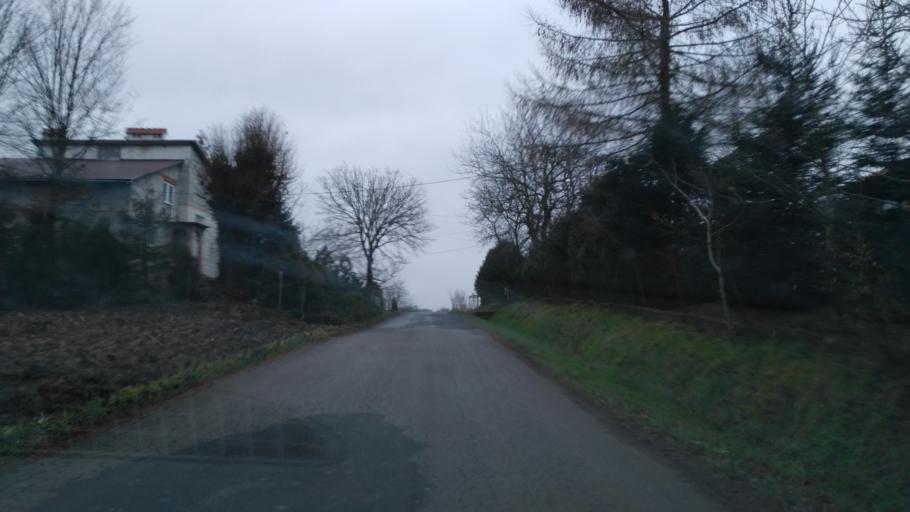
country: PL
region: Subcarpathian Voivodeship
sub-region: Powiat jaroslawski
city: Pruchnik
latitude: 49.9366
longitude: 22.5536
